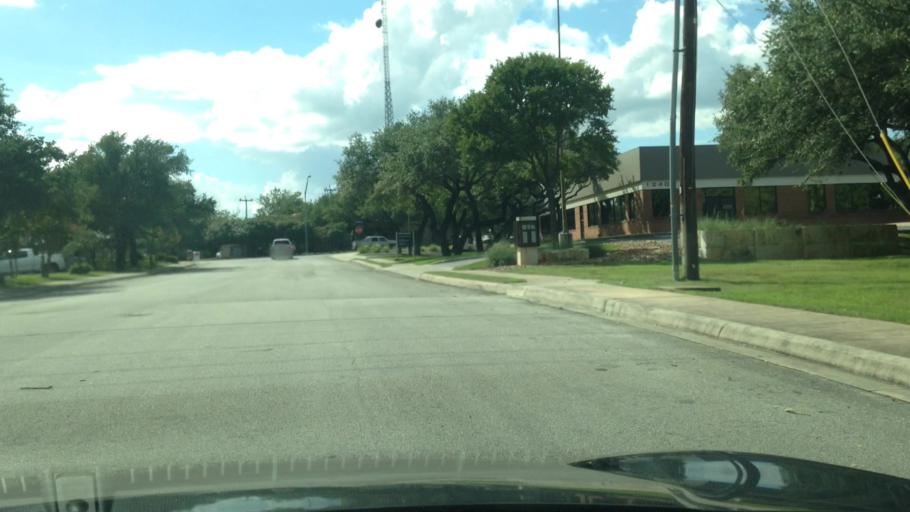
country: US
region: Texas
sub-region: Bexar County
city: Shavano Park
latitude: 29.5489
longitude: -98.5880
